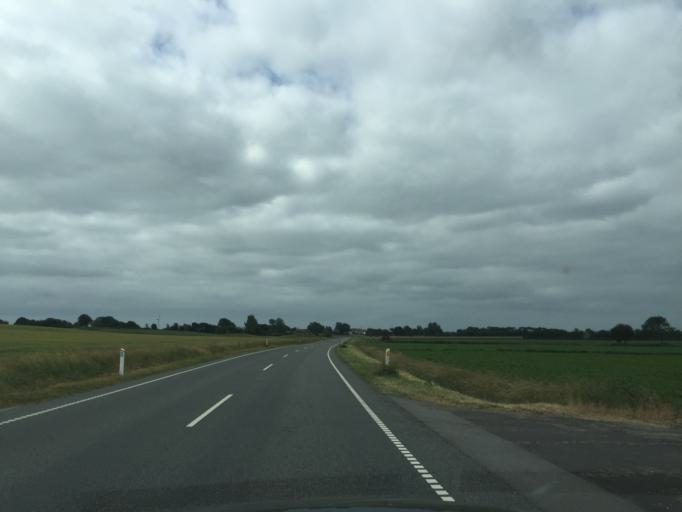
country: DK
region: South Denmark
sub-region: Vejen Kommune
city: Holsted
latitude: 55.4088
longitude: 8.9393
